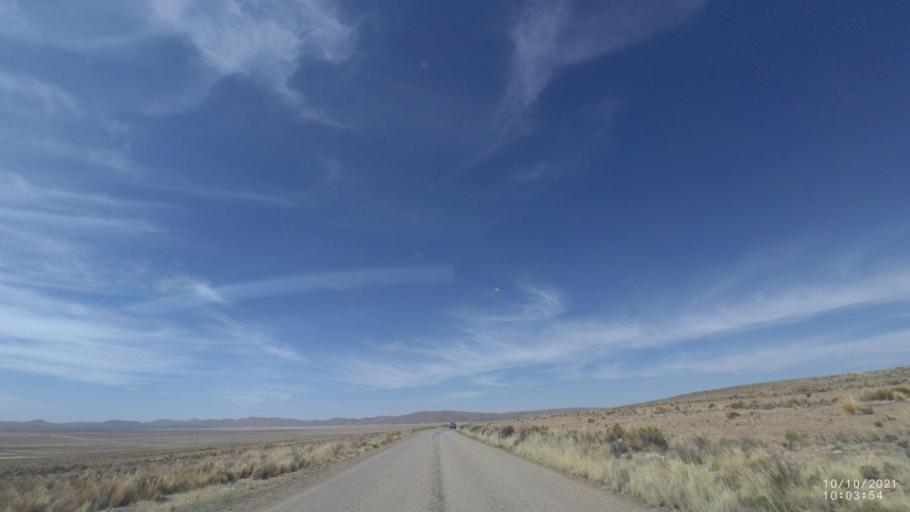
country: BO
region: La Paz
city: Eucaliptus
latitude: -17.3764
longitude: -67.4414
